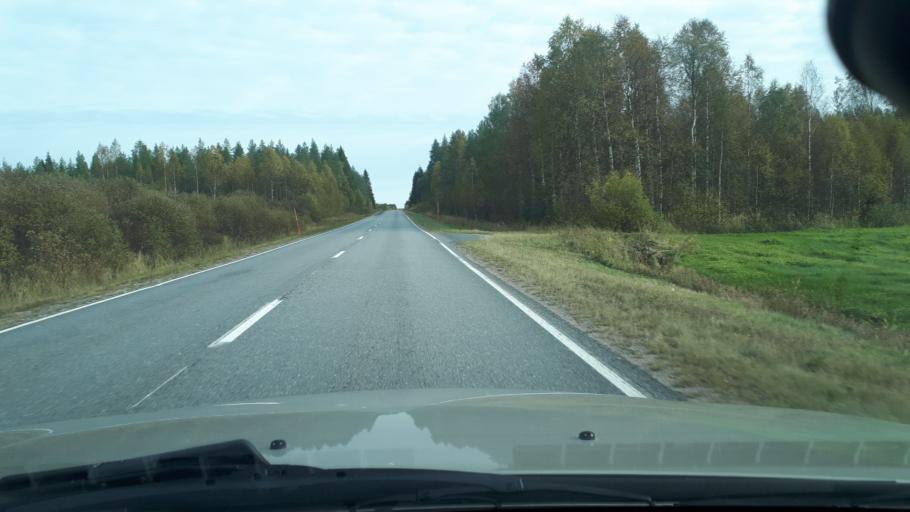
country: FI
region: Lapland
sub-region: Rovaniemi
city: Ranua
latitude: 65.9654
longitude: 26.0833
